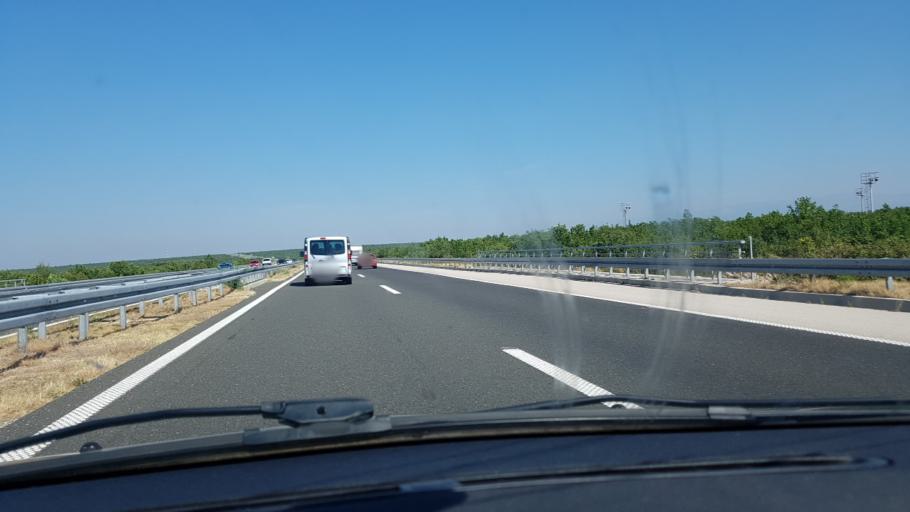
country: HR
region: Zadarska
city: Benkovac
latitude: 43.9876
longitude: 15.6279
